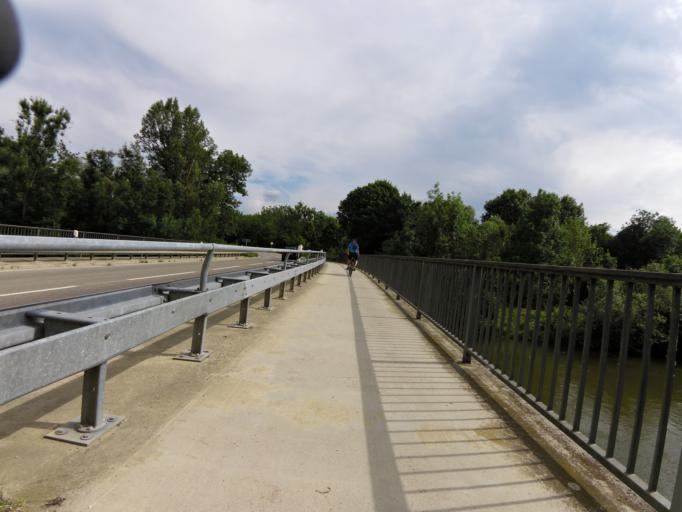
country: DE
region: Bavaria
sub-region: Upper Bavaria
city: Hebertshausen
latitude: 48.2971
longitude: 11.4926
